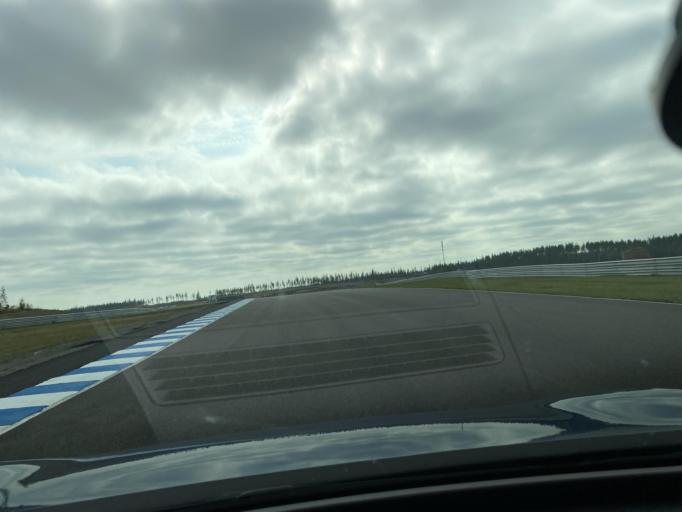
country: FI
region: Kymenlaakso
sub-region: Kouvola
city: Iitti
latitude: 60.8834
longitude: 26.4782
